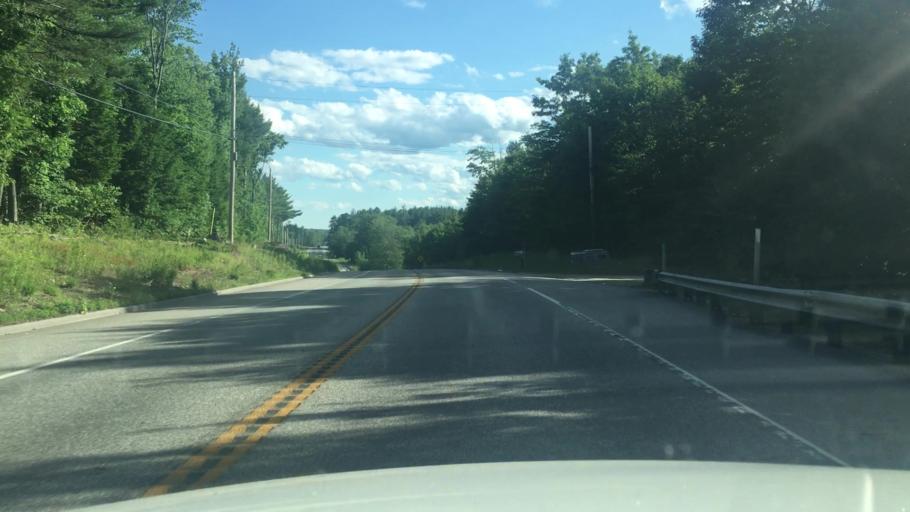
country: US
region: Maine
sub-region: Androscoggin County
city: Livermore
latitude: 44.4122
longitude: -70.2221
